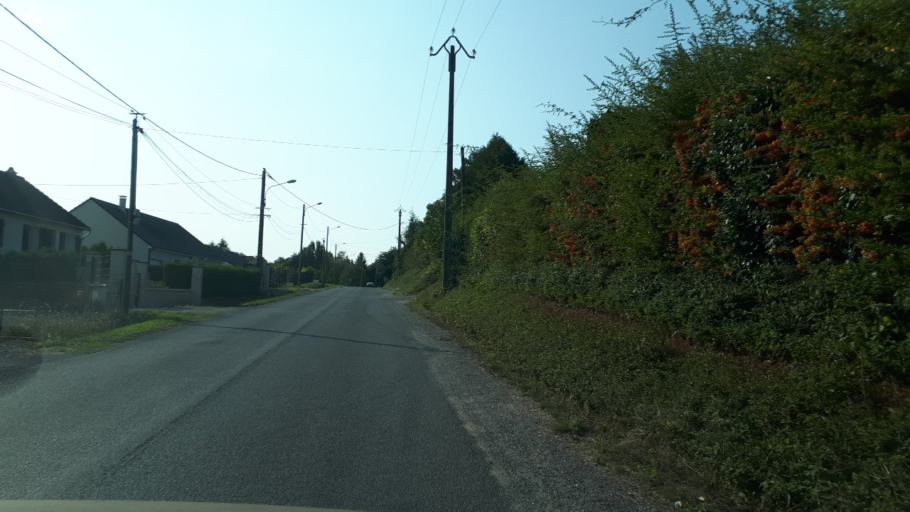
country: FR
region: Centre
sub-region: Departement du Cher
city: Vasselay
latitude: 47.2053
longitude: 2.4095
